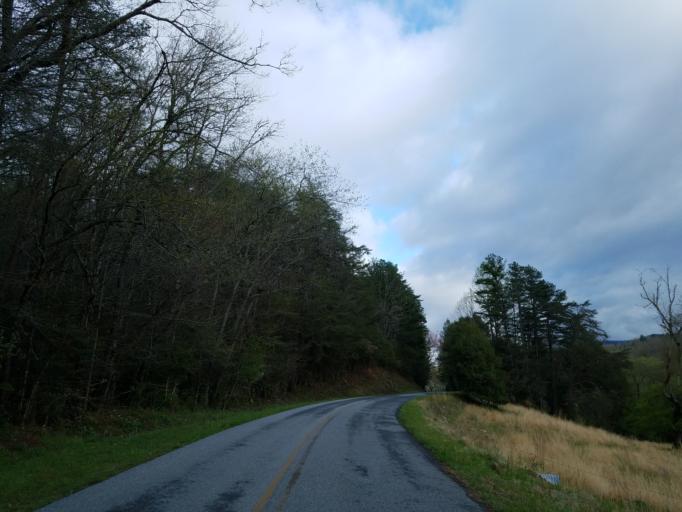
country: US
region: Georgia
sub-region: Fannin County
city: Blue Ridge
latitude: 34.7625
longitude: -84.2210
